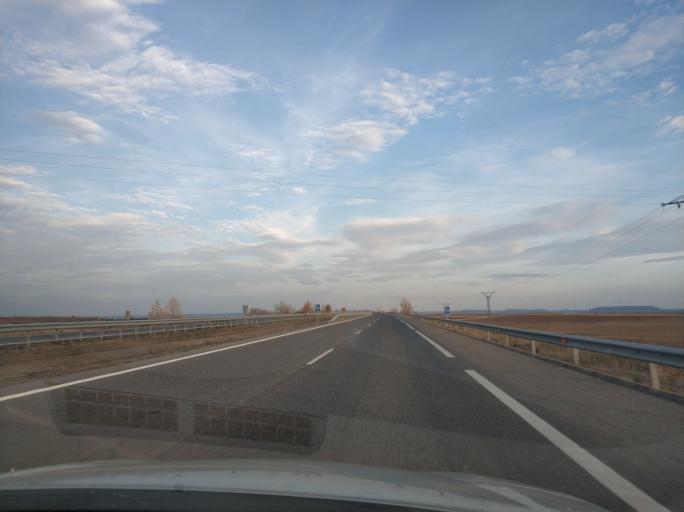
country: ES
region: Castille and Leon
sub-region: Provincia de Burgos
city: Padilla de Abajo
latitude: 42.4016
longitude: -4.1698
